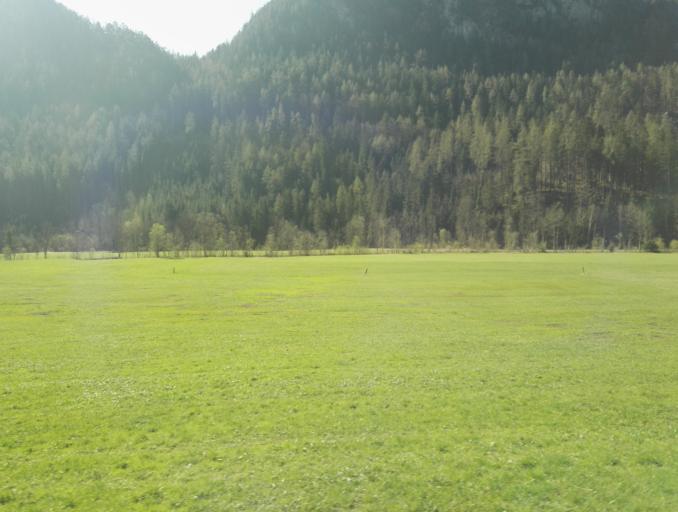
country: AT
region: Salzburg
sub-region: Politischer Bezirk Sankt Johann im Pongau
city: Forstau
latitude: 47.3973
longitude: 13.5291
